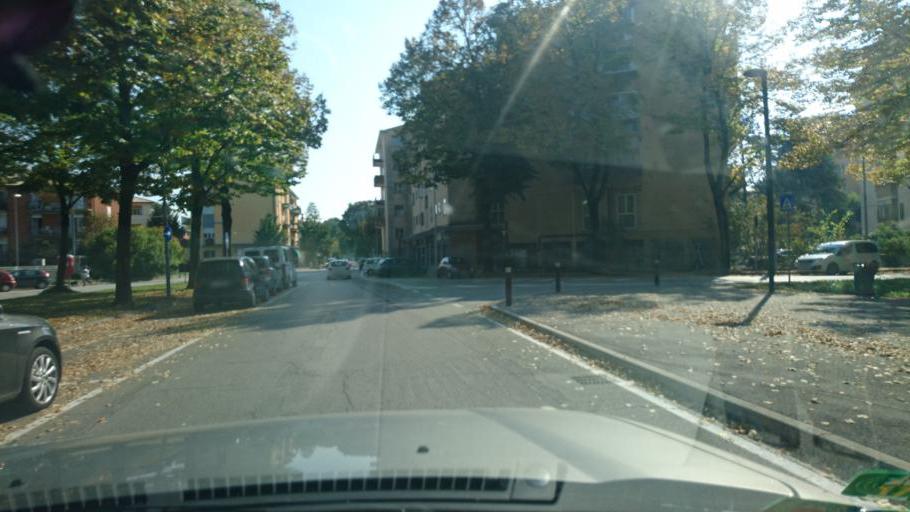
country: IT
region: Veneto
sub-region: Provincia di Padova
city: Caselle
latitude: 45.3999
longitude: 11.8294
